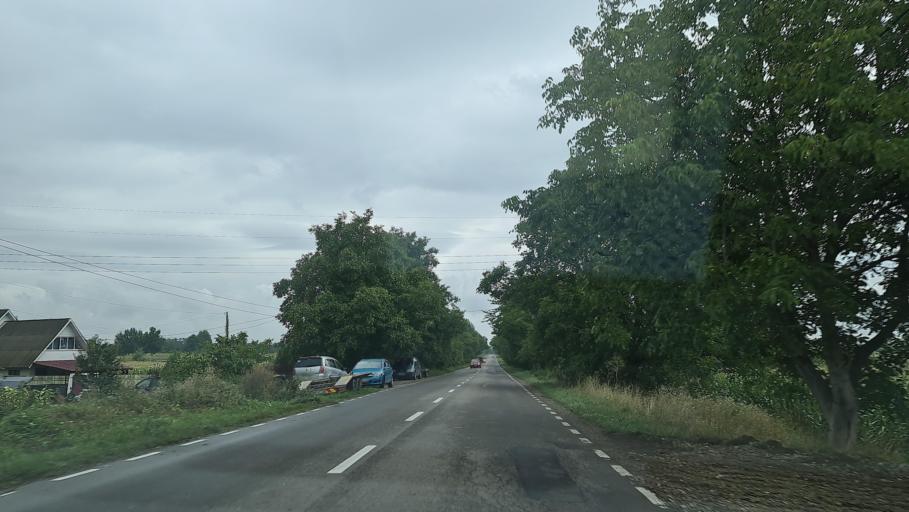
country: RO
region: Neamt
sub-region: Comuna Borlesti
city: Borlesti
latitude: 46.7636
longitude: 26.4708
